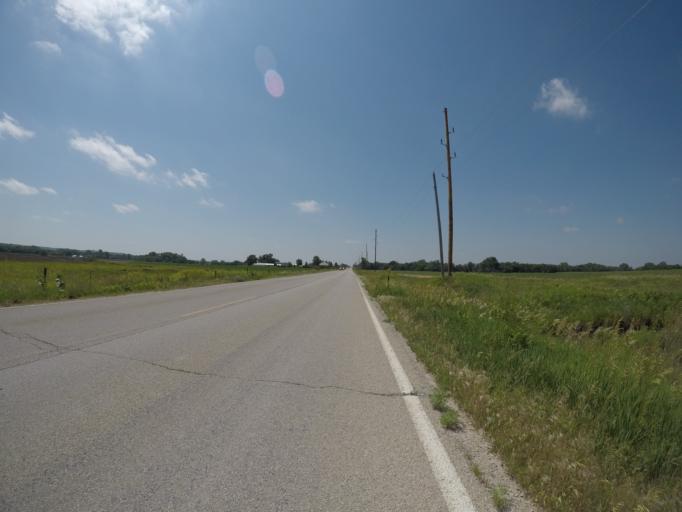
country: US
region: Kansas
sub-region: Pottawatomie County
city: Westmoreland
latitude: 39.3331
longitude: -96.4361
